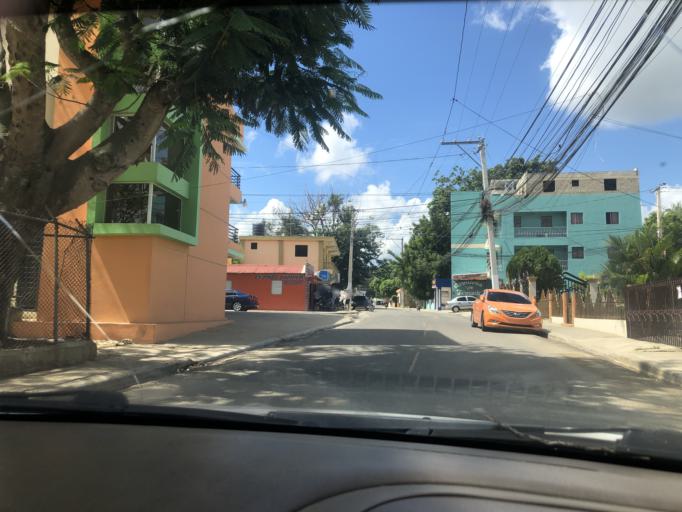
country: DO
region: Santiago
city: Santiago de los Caballeros
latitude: 19.4127
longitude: -70.7097
